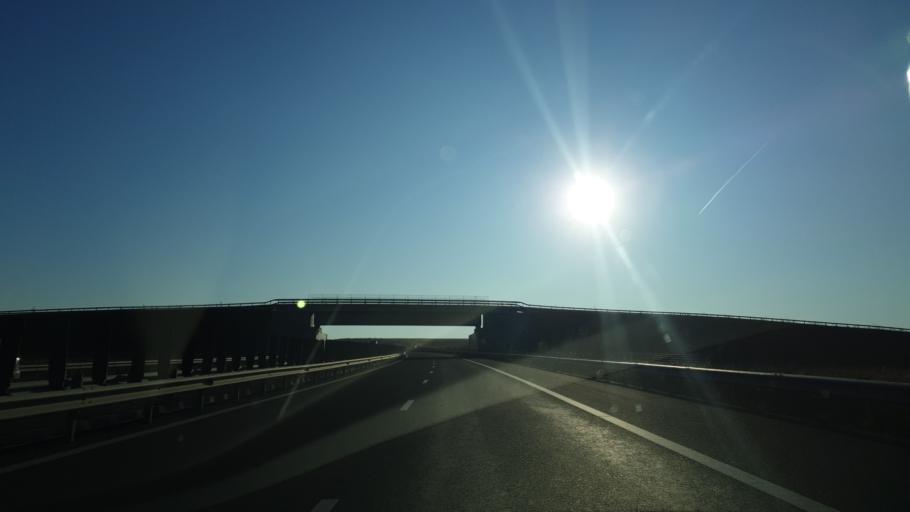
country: RO
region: Timis
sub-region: Comuna Costeiu
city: Costeiu
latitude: 45.7429
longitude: 21.8780
